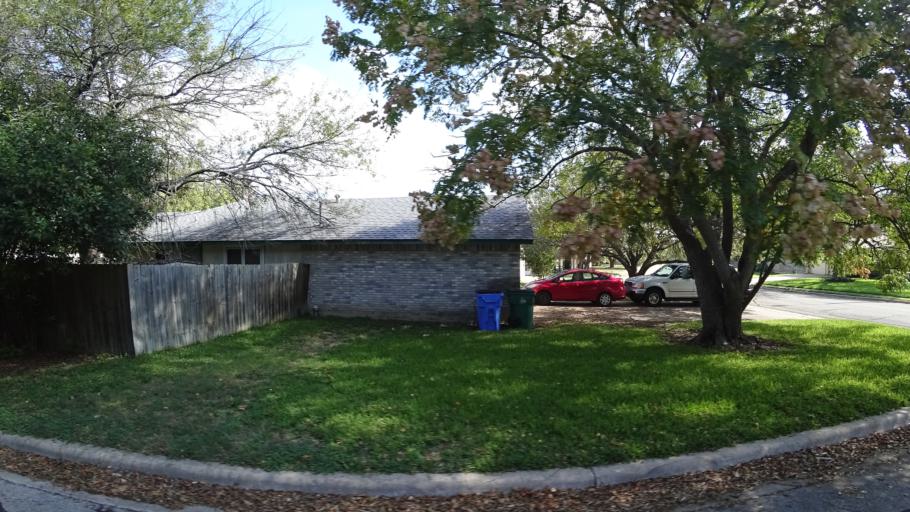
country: US
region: Texas
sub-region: Travis County
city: Windemere
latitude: 30.4558
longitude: -97.6447
